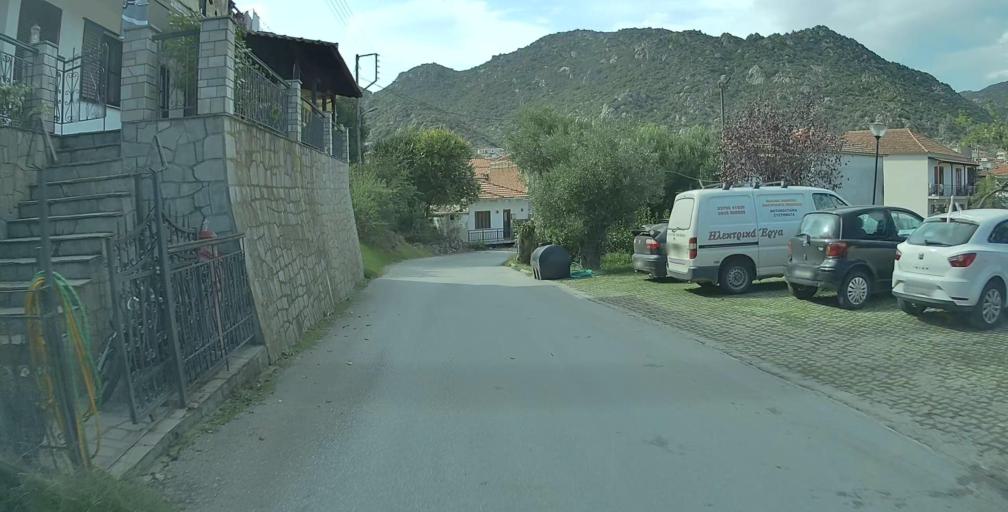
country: GR
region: Central Macedonia
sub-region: Nomos Chalkidikis
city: Sykia
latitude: 40.0378
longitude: 23.9430
